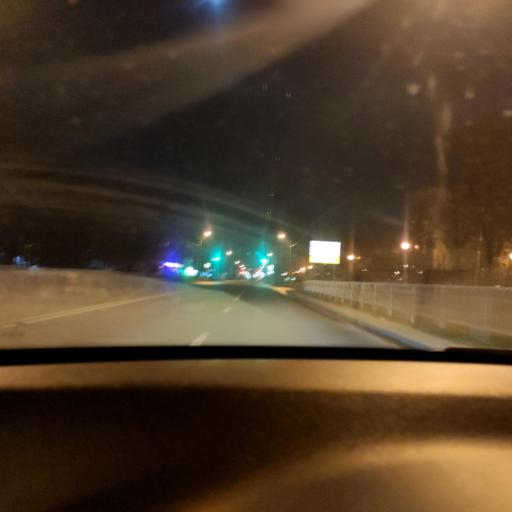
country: RU
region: Samara
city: Samara
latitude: 53.2323
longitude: 50.2146
